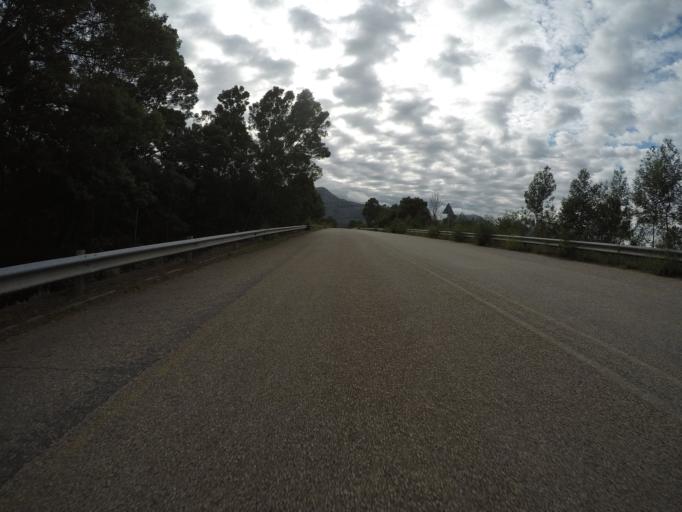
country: ZA
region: Eastern Cape
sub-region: Cacadu District Municipality
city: Kareedouw
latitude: -34.0144
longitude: 24.3057
